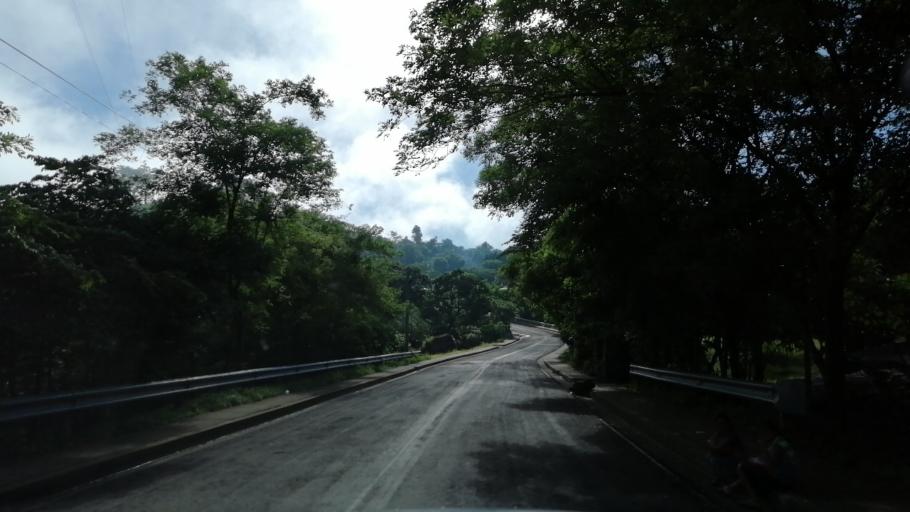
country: SV
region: Morazan
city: Cacaopera
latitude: 13.7745
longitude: -88.0867
